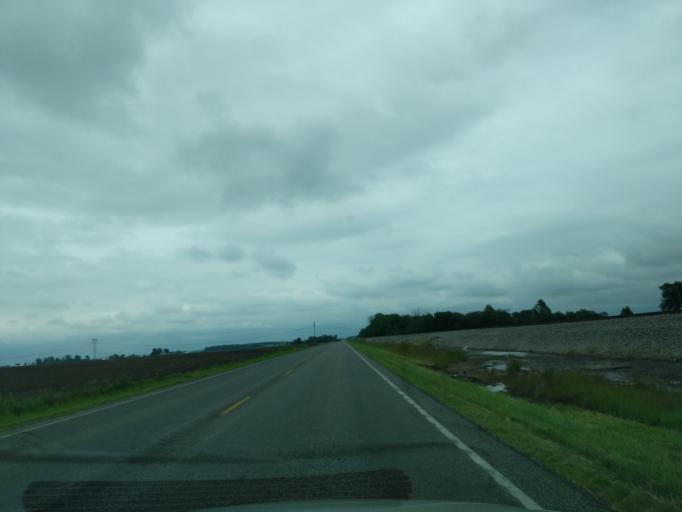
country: US
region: Indiana
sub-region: Madison County
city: Elwood
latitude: 40.2805
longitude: -85.9182
